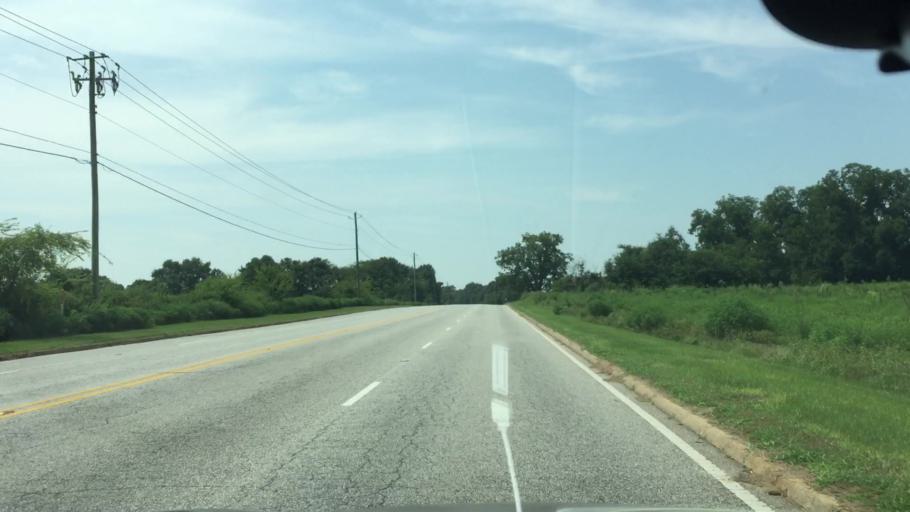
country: US
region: Alabama
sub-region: Coffee County
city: Enterprise
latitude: 31.3451
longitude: -85.8379
